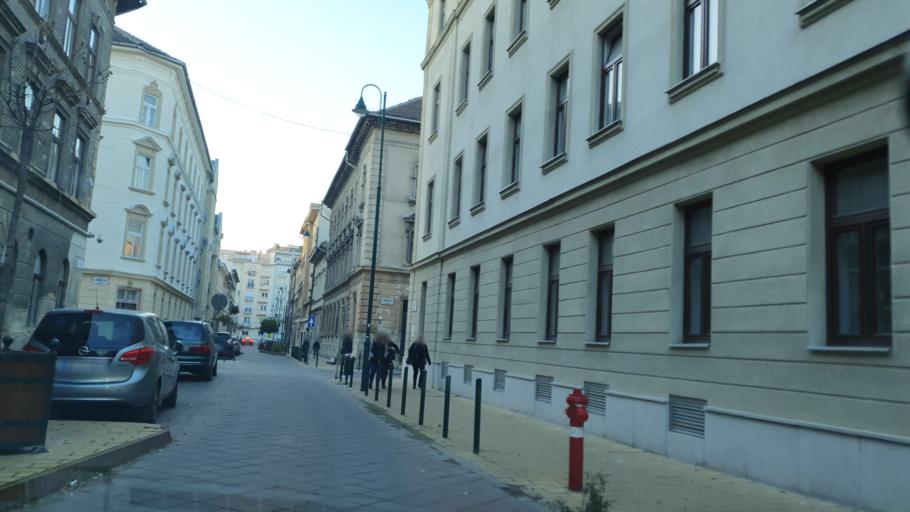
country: HU
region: Budapest
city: Budapest IX. keruelet
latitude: 47.4779
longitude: 19.0776
